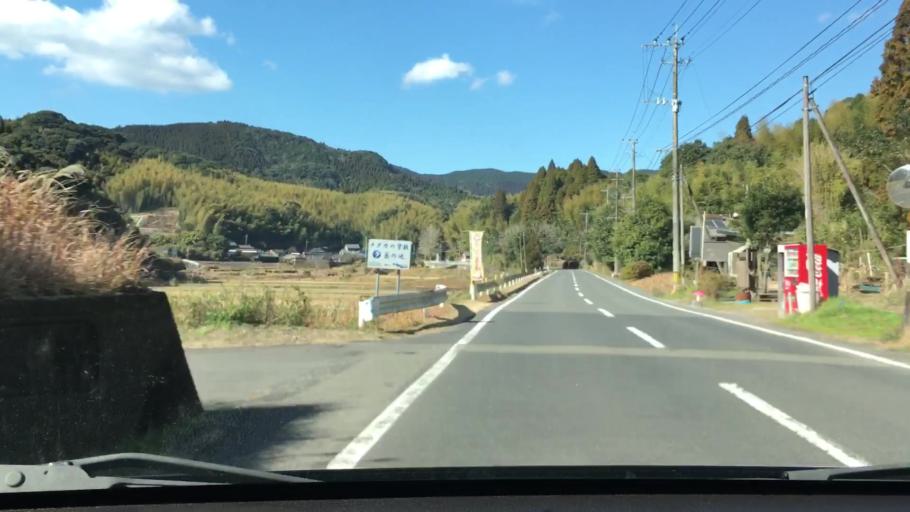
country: JP
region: Kagoshima
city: Ijuin
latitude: 31.7052
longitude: 130.4460
